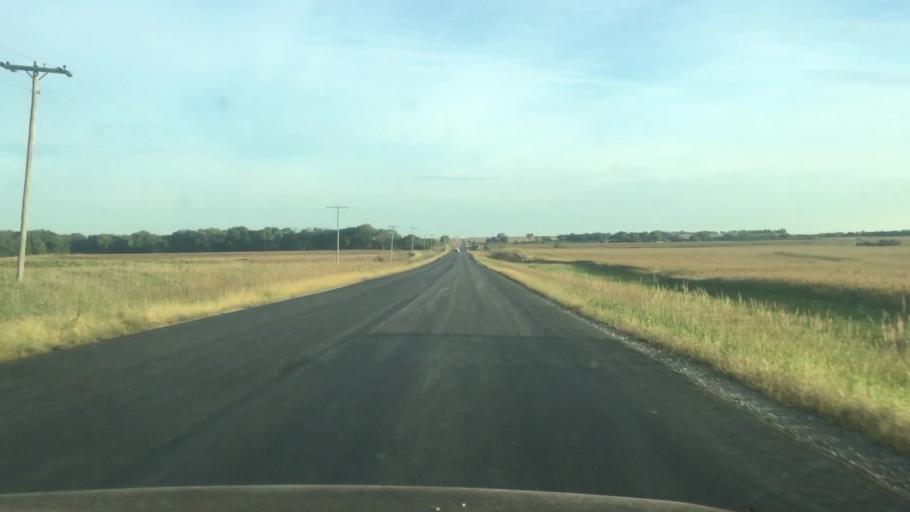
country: US
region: Kansas
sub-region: Marshall County
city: Marysville
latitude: 39.8712
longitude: -96.6011
